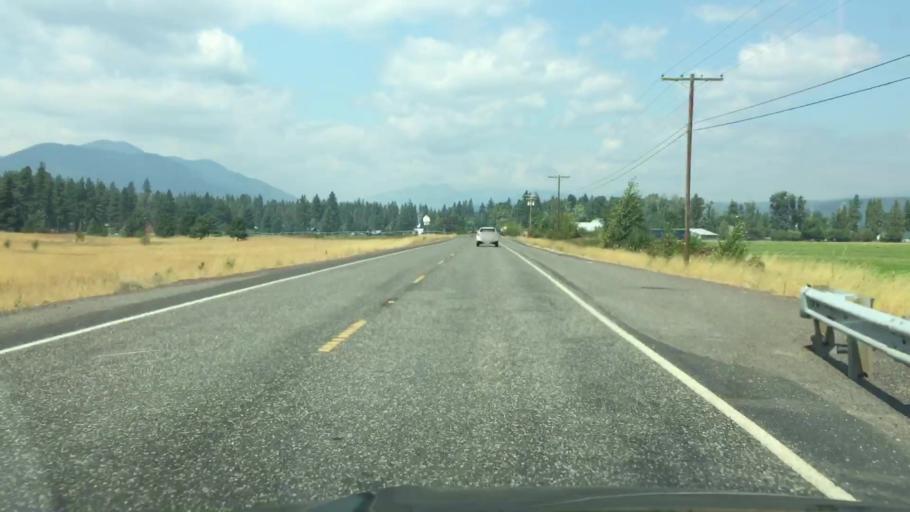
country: US
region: Washington
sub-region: Klickitat County
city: White Salmon
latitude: 45.9909
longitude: -121.5195
